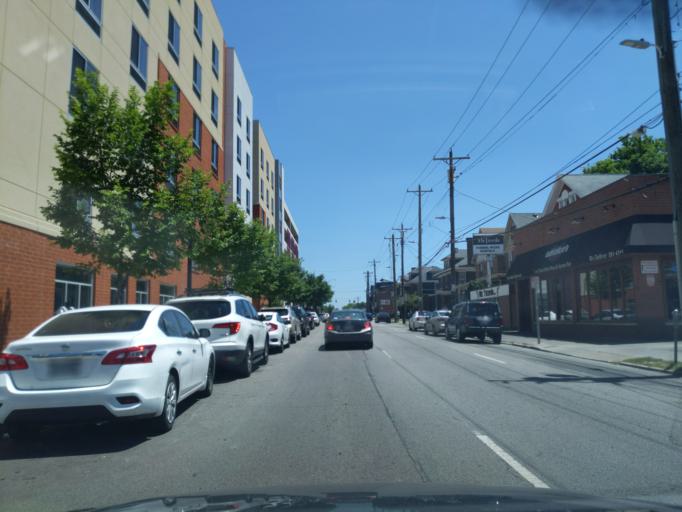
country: US
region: Kentucky
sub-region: Campbell County
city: Newport
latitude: 39.1277
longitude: -84.5166
